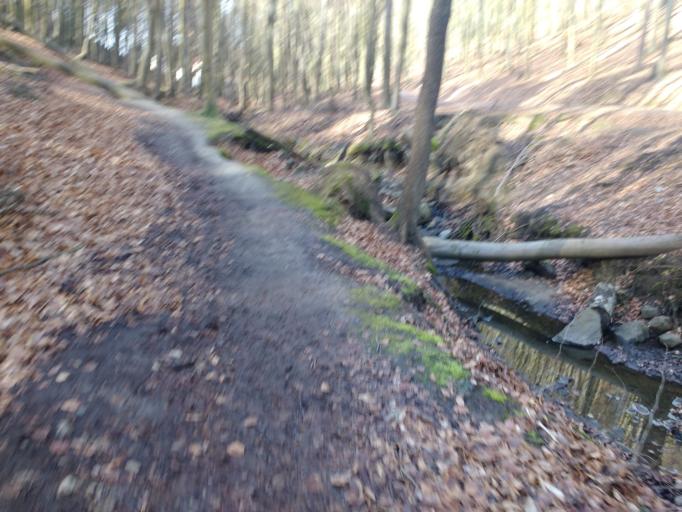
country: PL
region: Pomeranian Voivodeship
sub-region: Gdynia
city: Wielki Kack
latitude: 54.4799
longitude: 18.5149
